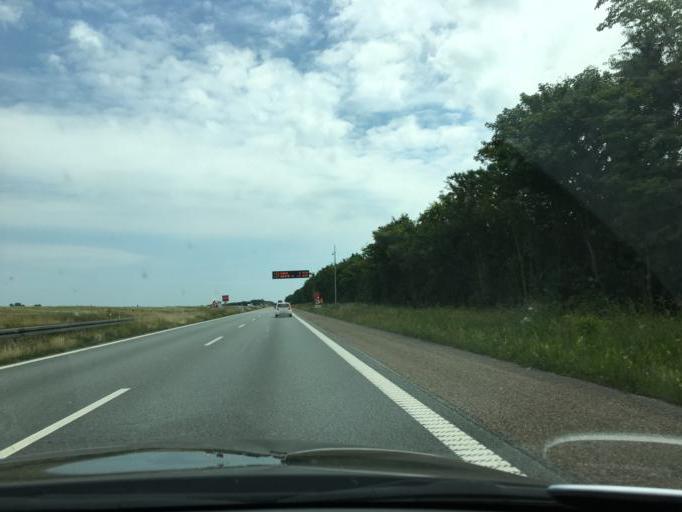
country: DK
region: Zealand
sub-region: Koge Kommune
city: Ejby
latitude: 55.4796
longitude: 12.1179
